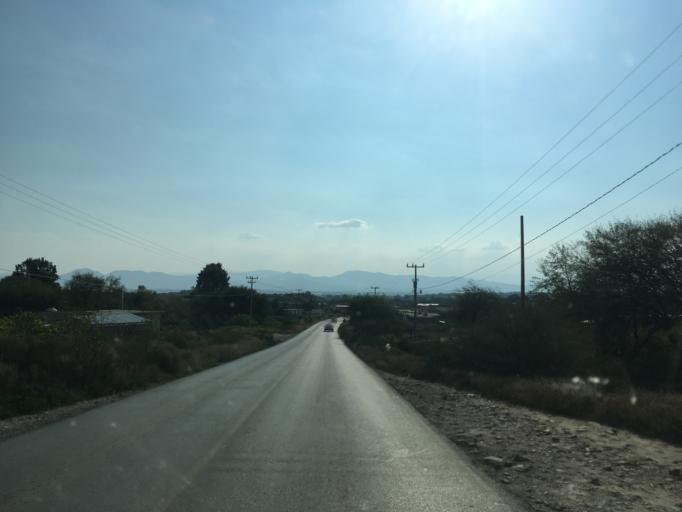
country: MX
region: Hidalgo
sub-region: Ixmiquilpan
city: El Nith
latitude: 20.5585
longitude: -99.1565
